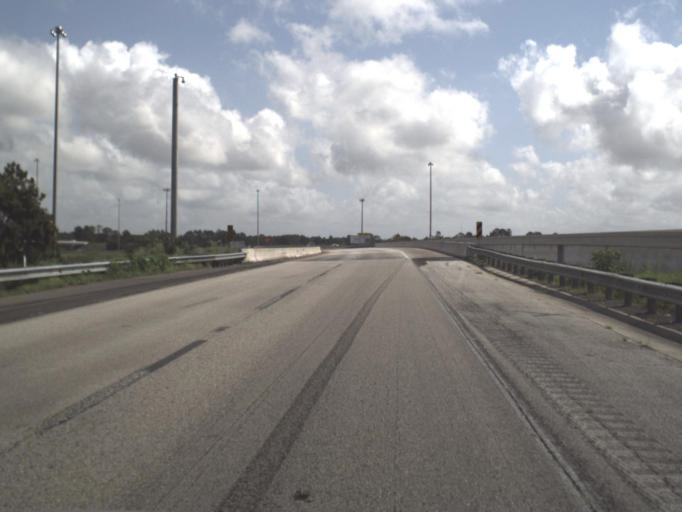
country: US
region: Florida
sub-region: Hillsborough County
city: Pebble Creek
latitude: 28.1656
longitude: -82.3960
